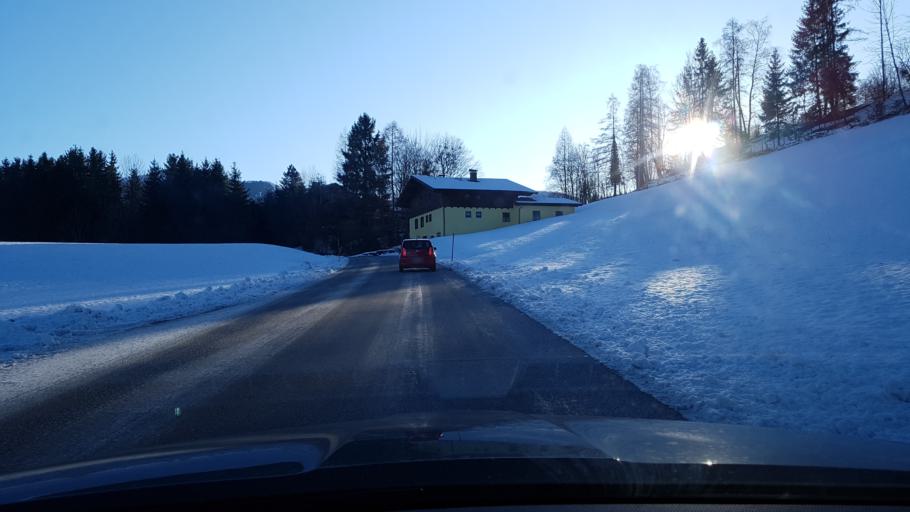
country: AT
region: Salzburg
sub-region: Politischer Bezirk Hallein
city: Kuchl
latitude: 47.6541
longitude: 13.1985
